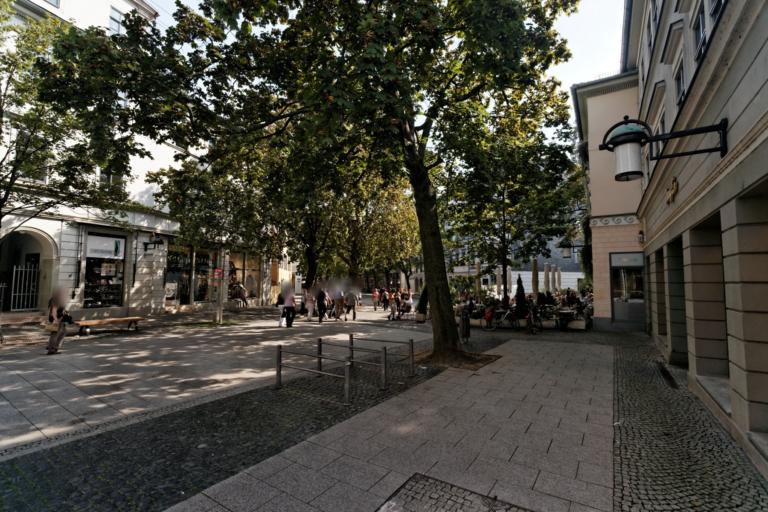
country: DE
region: Thuringia
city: Weimar
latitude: 50.9790
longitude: 11.3272
